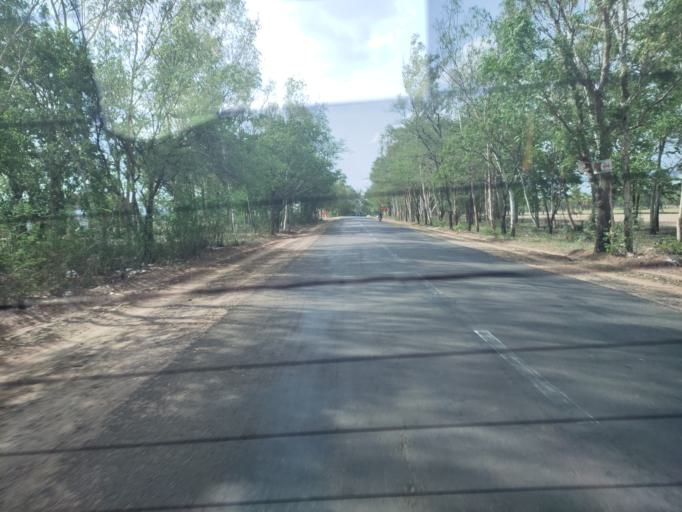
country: MM
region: Magway
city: Magway
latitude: 20.2296
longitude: 95.0180
